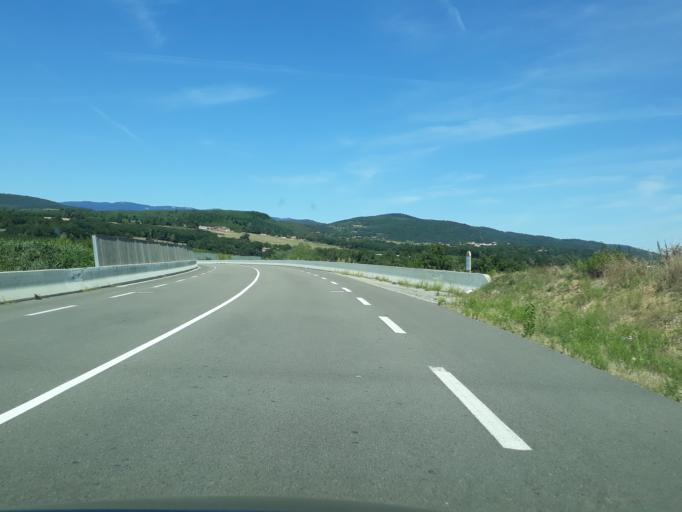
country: FR
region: Rhone-Alpes
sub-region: Departement de l'Ardeche
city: Davezieux
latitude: 45.2590
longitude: 4.7190
